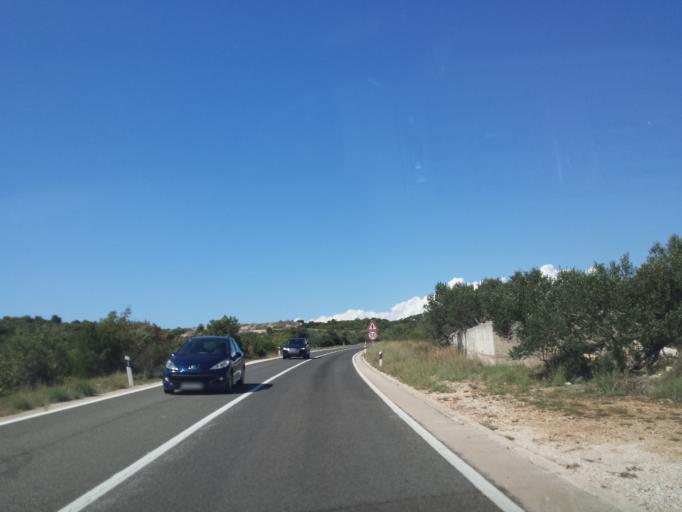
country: HR
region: Sibensko-Kniniska
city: Rogoznica
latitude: 43.5469
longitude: 15.9612
